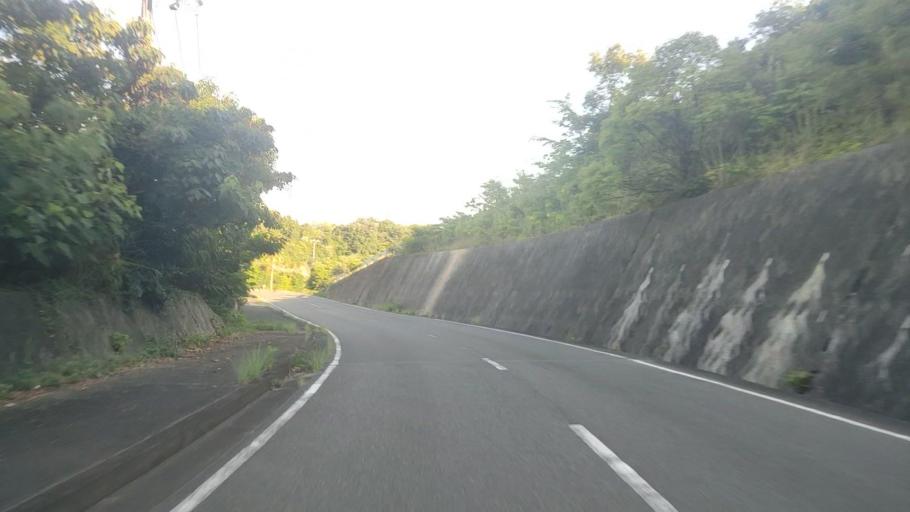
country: JP
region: Wakayama
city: Tanabe
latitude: 33.7732
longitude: 135.3056
